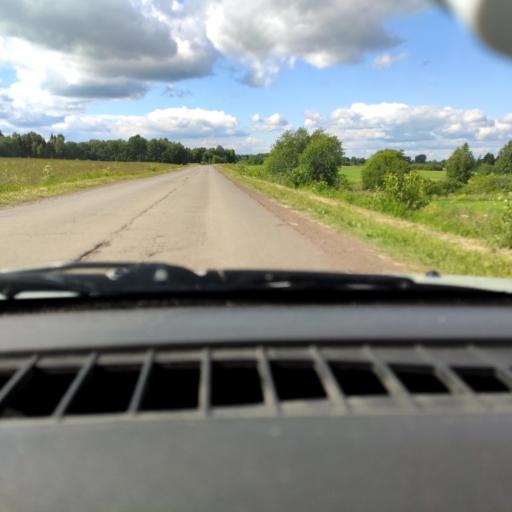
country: RU
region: Perm
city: Uinskoye
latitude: 57.1575
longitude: 56.5713
